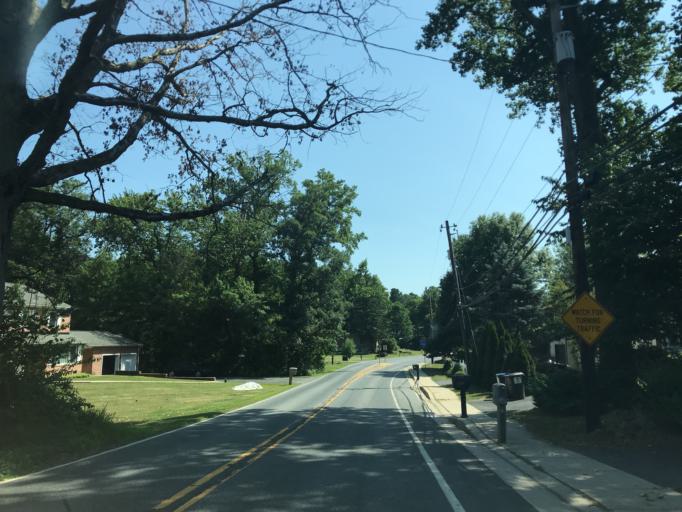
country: US
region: Delaware
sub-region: New Castle County
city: Claymont
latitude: 39.8348
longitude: -75.5194
